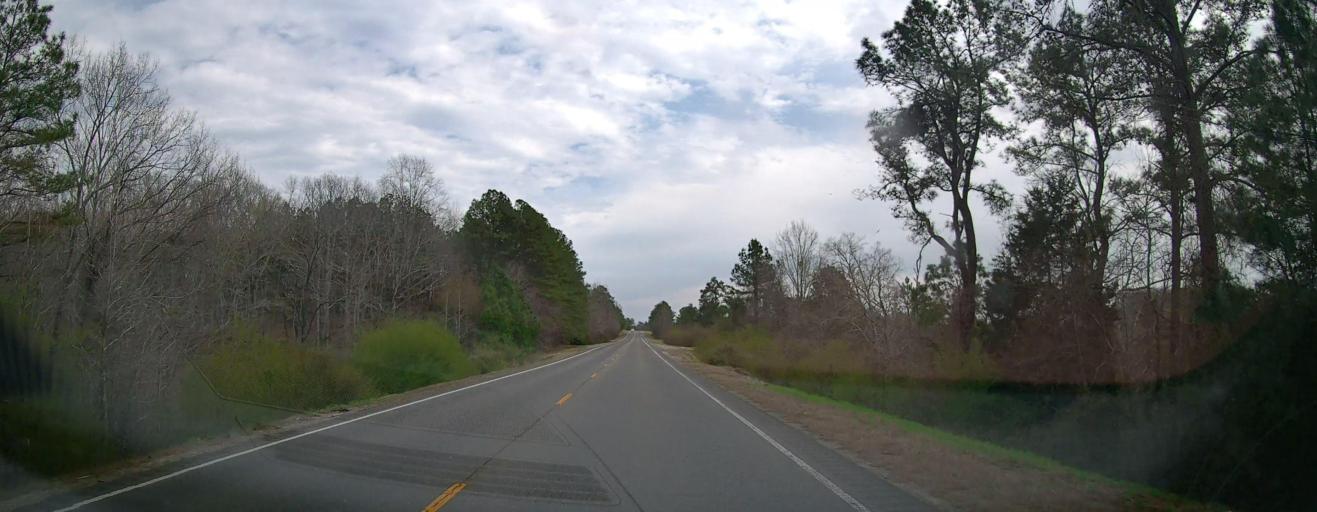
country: US
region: Alabama
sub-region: Marion County
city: Guin
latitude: 34.0433
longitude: -87.9568
